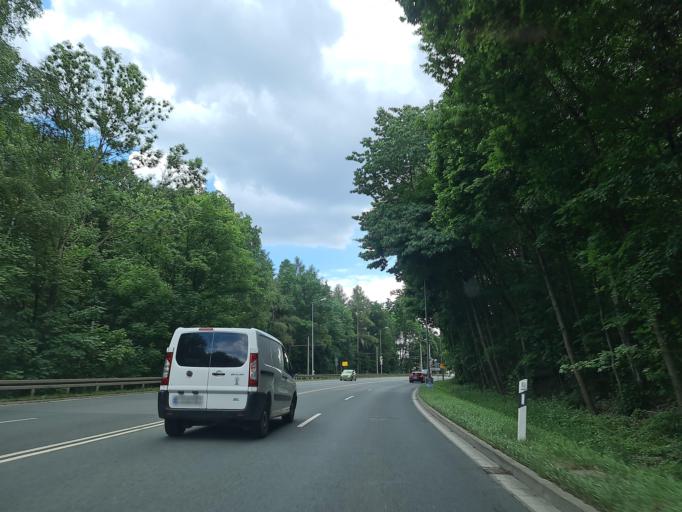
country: DE
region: Saxony
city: Plauen
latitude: 50.5188
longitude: 12.1193
